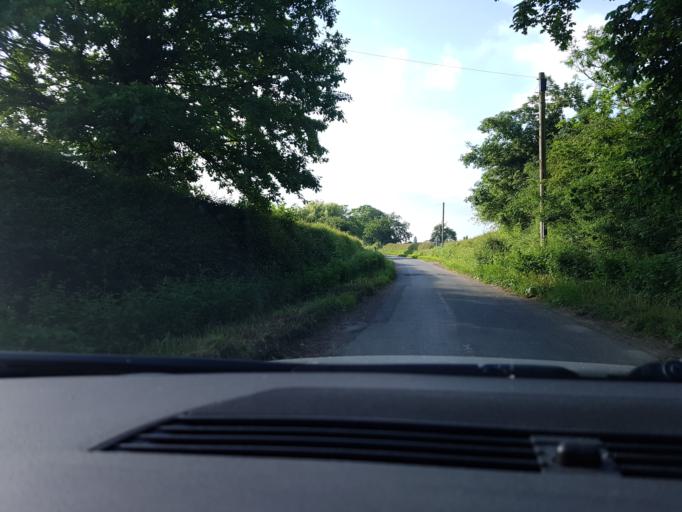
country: GB
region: England
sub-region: Northamptonshire
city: Deanshanger
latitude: 52.0399
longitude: -0.9118
